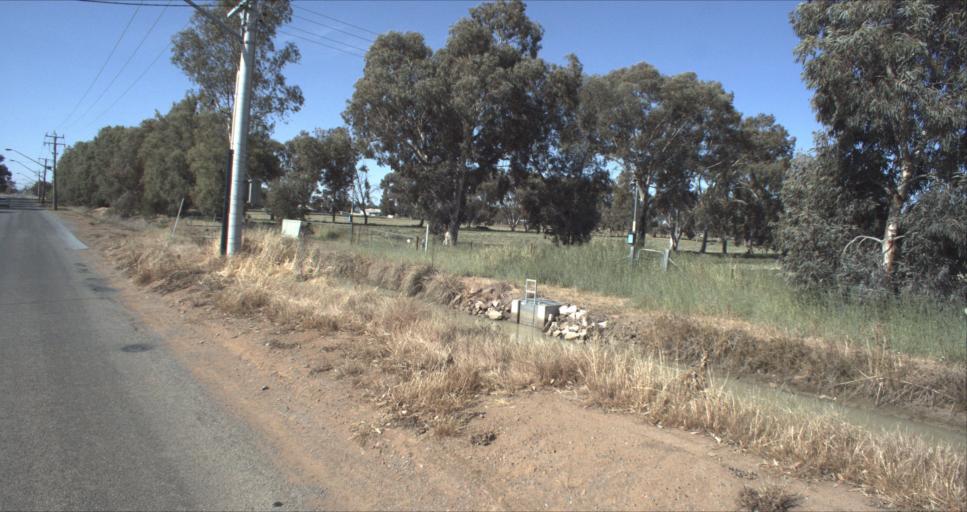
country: AU
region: New South Wales
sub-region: Leeton
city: Leeton
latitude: -34.5666
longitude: 146.4143
